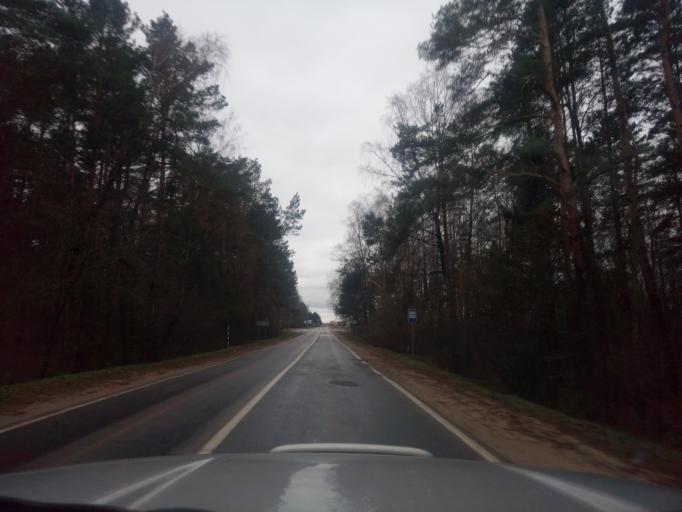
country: BY
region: Minsk
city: Kapyl'
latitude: 53.1581
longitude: 27.1064
